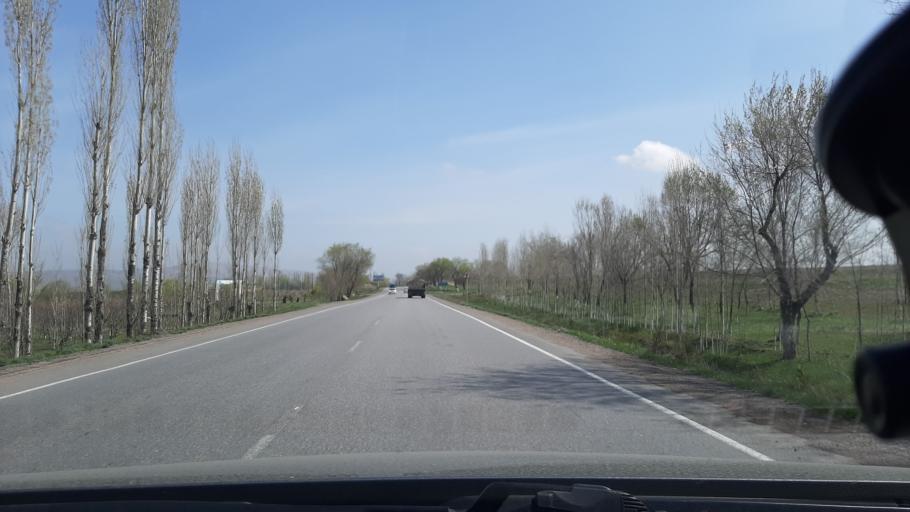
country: TJ
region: Viloyati Sughd
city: Shahriston
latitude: 39.7987
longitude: 68.8840
